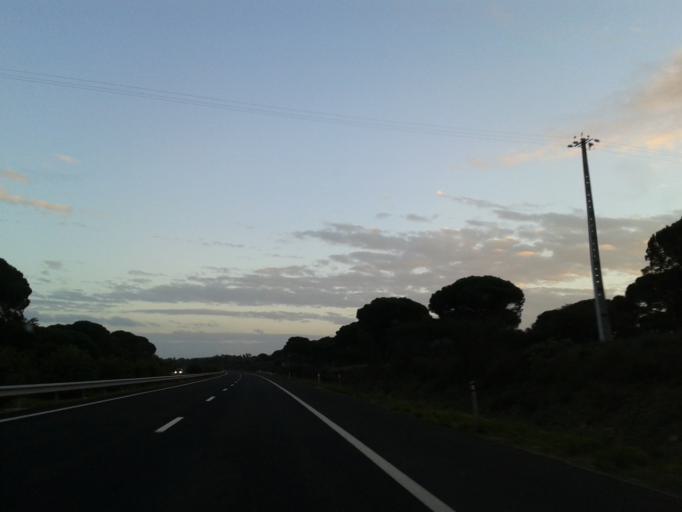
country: PT
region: Santarem
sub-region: Benavente
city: Poceirao
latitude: 38.7428
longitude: -8.6818
